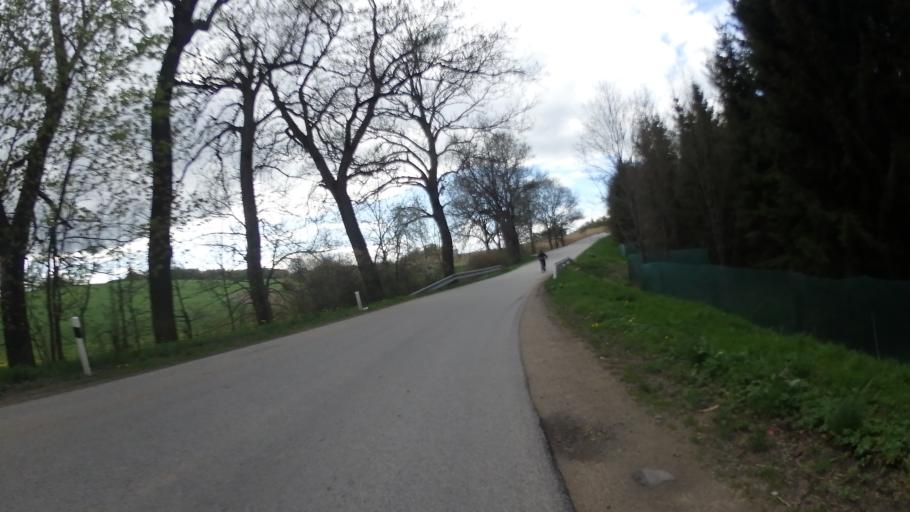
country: CZ
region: Vysocina
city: Merin
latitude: 49.3639
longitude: 15.9027
